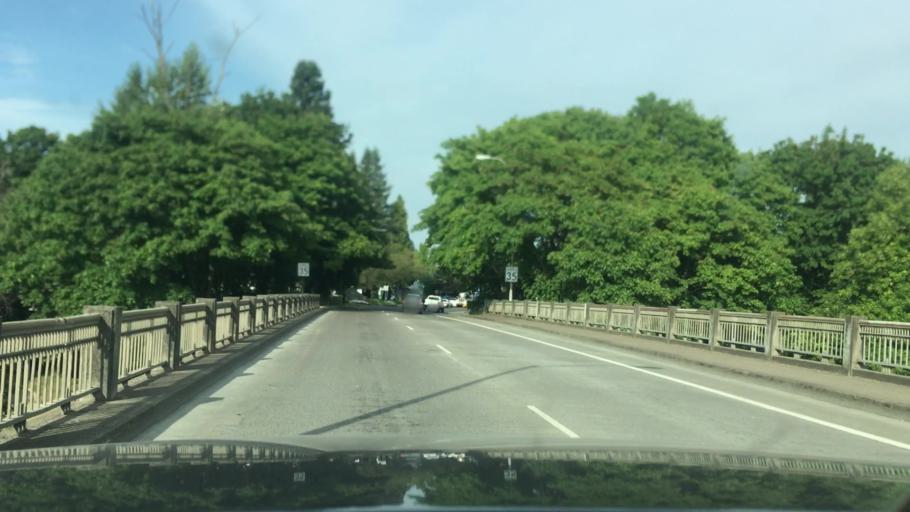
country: US
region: Oregon
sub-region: Lane County
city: Springfield
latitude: 44.0453
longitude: -123.0268
